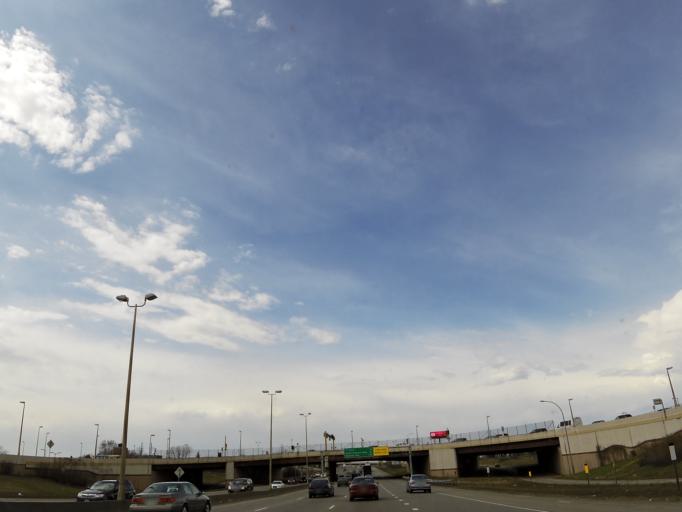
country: US
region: Minnesota
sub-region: Hennepin County
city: Richfield
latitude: 44.8624
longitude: -93.2356
